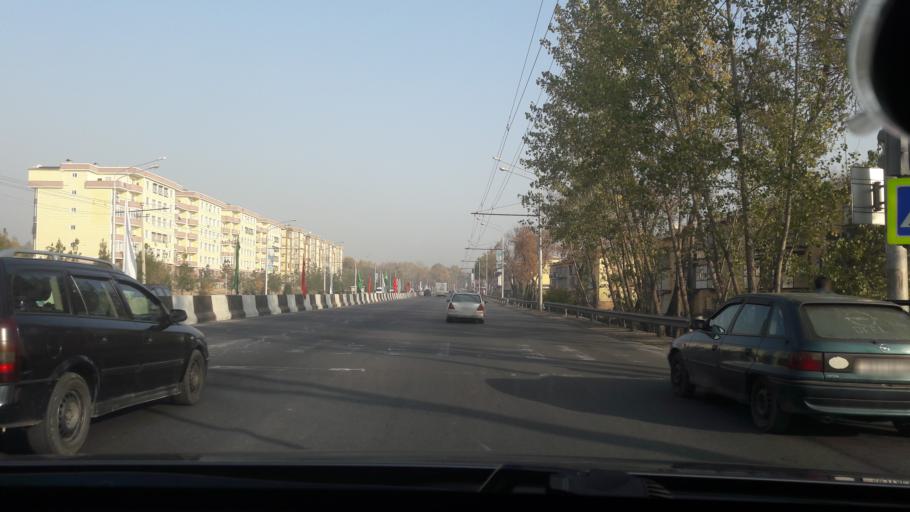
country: TJ
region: Dushanbe
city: Dushanbe
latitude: 38.5533
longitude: 68.8484
